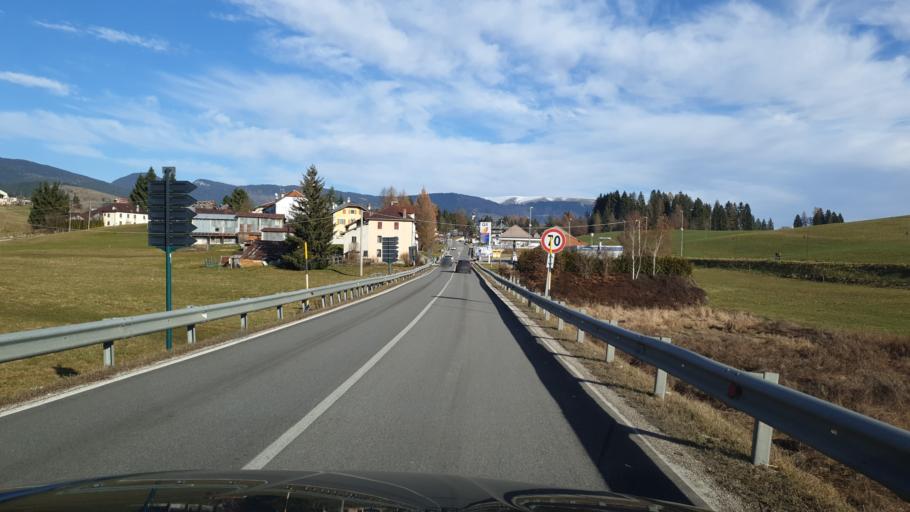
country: IT
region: Veneto
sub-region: Provincia di Vicenza
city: Asiago
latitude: 45.8692
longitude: 11.4969
